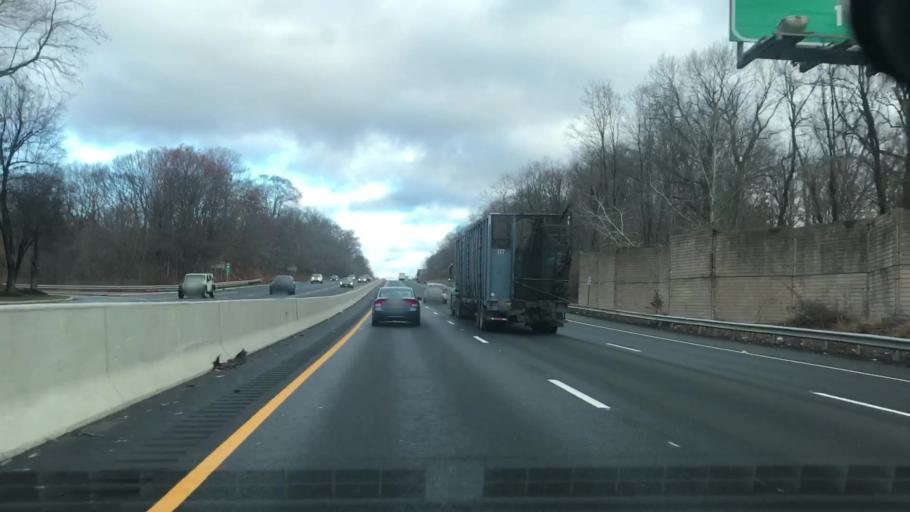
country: US
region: New Jersey
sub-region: Bergen County
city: Waldwick
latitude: 41.0183
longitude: -74.1080
